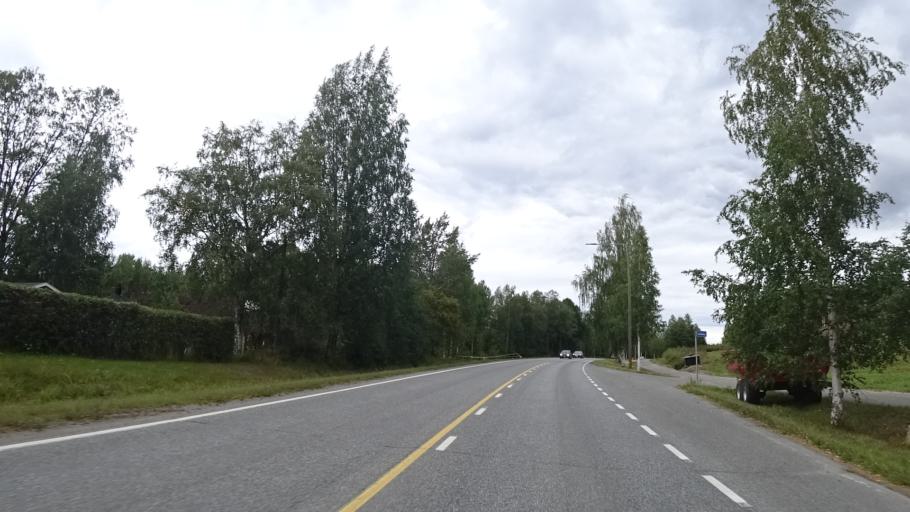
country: FI
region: North Karelia
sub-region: Joensuu
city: Ilomantsi
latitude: 62.6580
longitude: 30.9331
